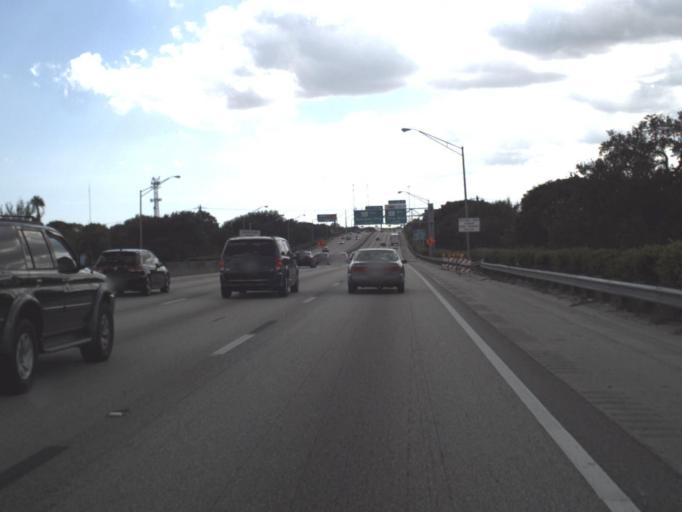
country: US
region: Florida
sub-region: Broward County
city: Pembroke Pines
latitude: 26.0237
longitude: -80.2132
